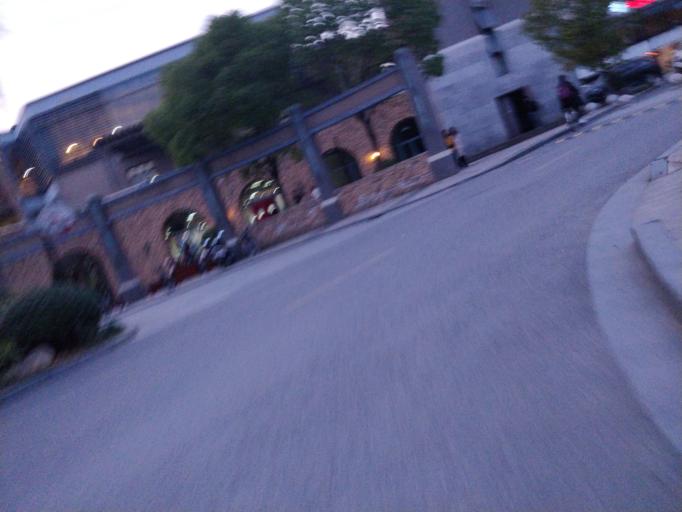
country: CN
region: Shanghai Shi
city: Huangdu
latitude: 31.2893
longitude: 121.2139
